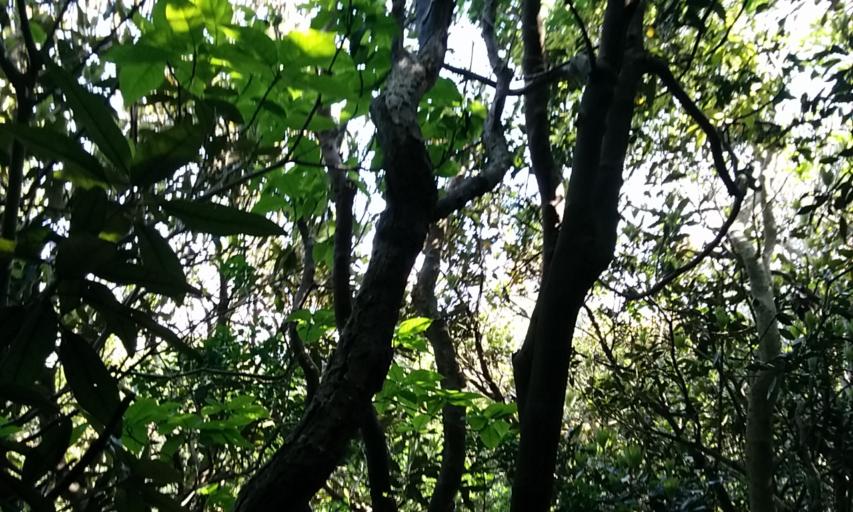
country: JP
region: Oita
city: Tsukumiura
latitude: 33.3462
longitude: 132.0209
